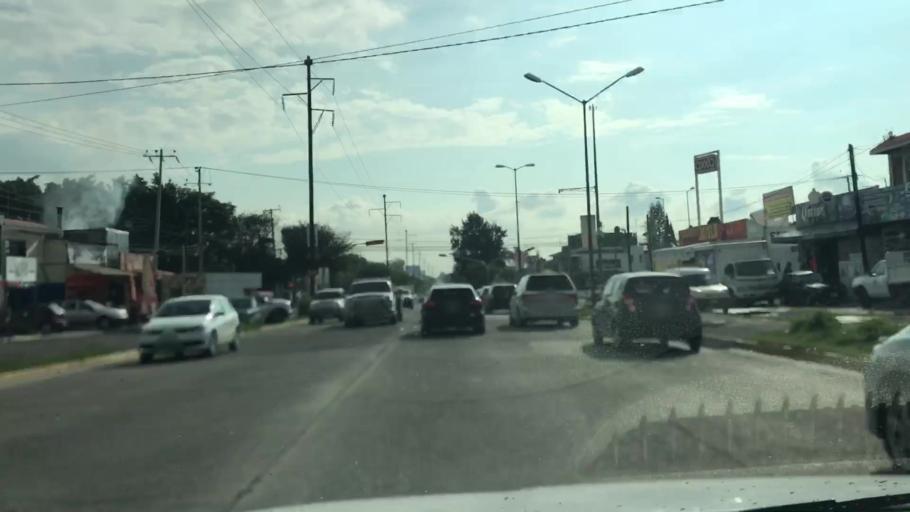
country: MX
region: Jalisco
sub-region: Tlajomulco de Zuniga
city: Palomar
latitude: 20.6301
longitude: -103.4446
